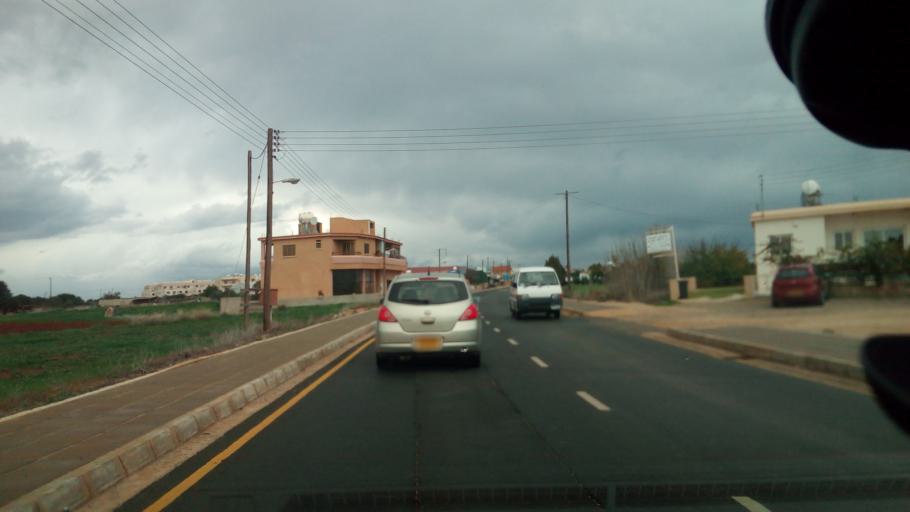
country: CY
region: Ammochostos
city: Liopetri
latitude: 35.0166
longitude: 33.8979
